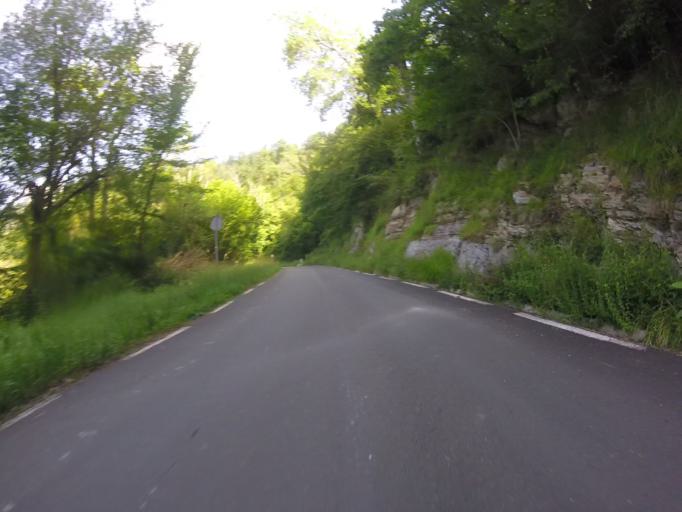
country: ES
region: Basque Country
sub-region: Provincia de Guipuzcoa
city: Beasain
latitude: 43.0829
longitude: -2.2295
